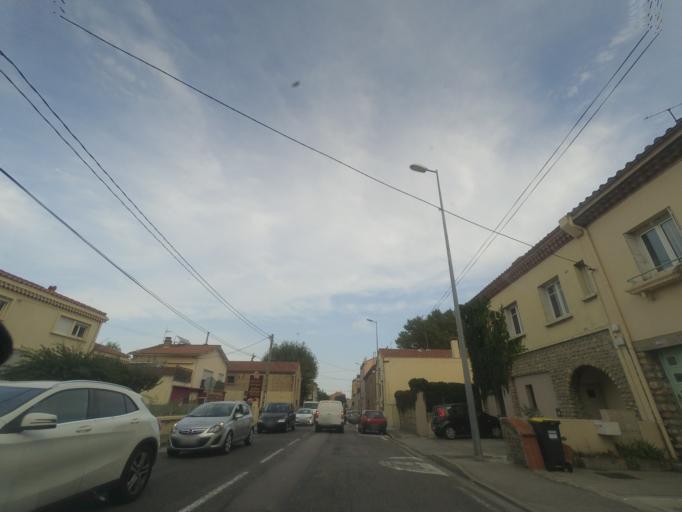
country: FR
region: Languedoc-Roussillon
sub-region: Departement des Pyrenees-Orientales
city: Perpignan
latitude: 42.6976
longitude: 2.8695
